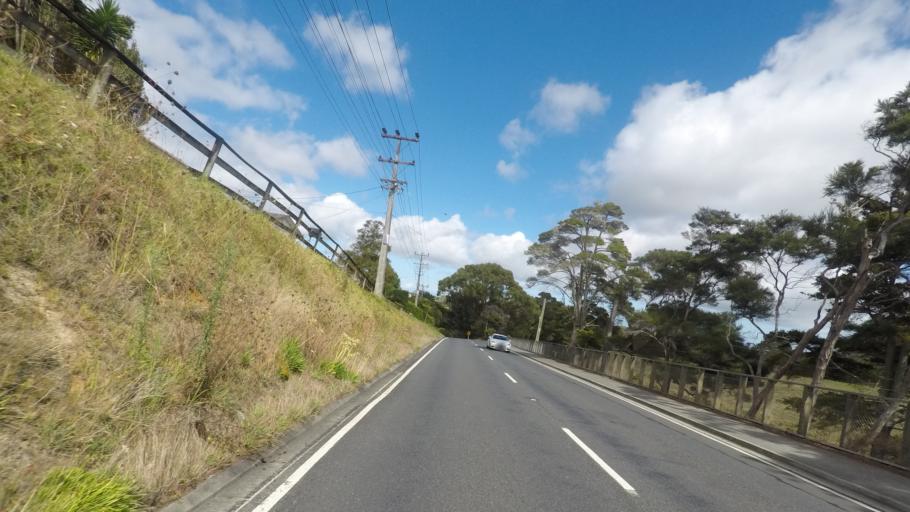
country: NZ
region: Auckland
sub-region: Auckland
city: Muriwai Beach
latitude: -36.7696
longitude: 174.5512
